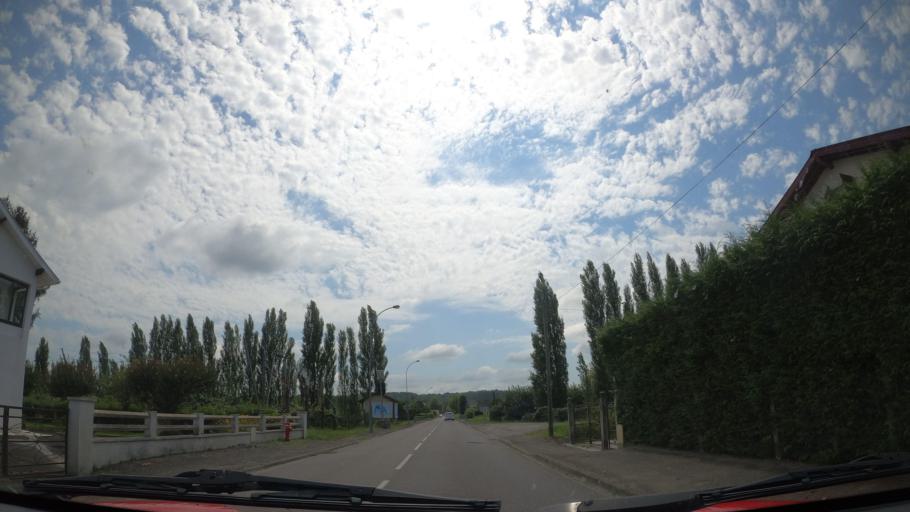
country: FR
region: Aquitaine
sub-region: Departement des Landes
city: Peyrehorade
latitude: 43.5392
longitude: -1.1074
